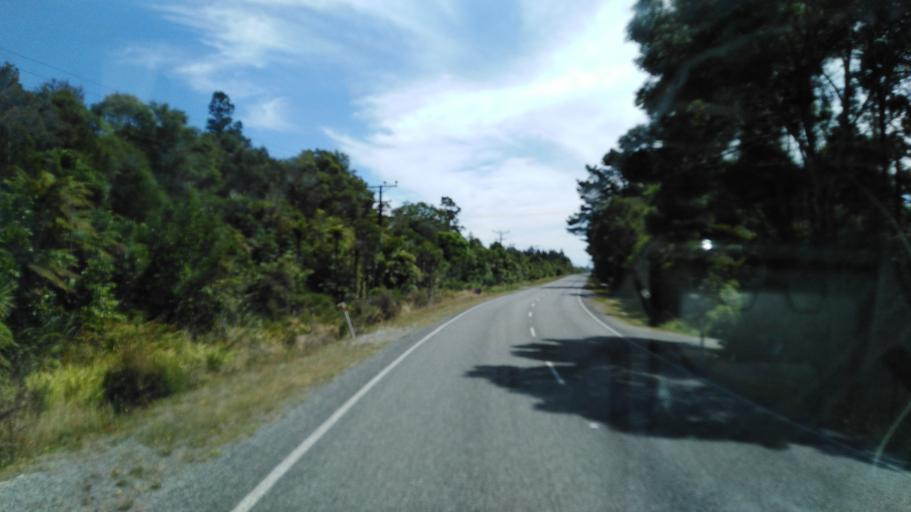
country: NZ
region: West Coast
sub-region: Buller District
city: Westport
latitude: -41.7460
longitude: 171.7197
